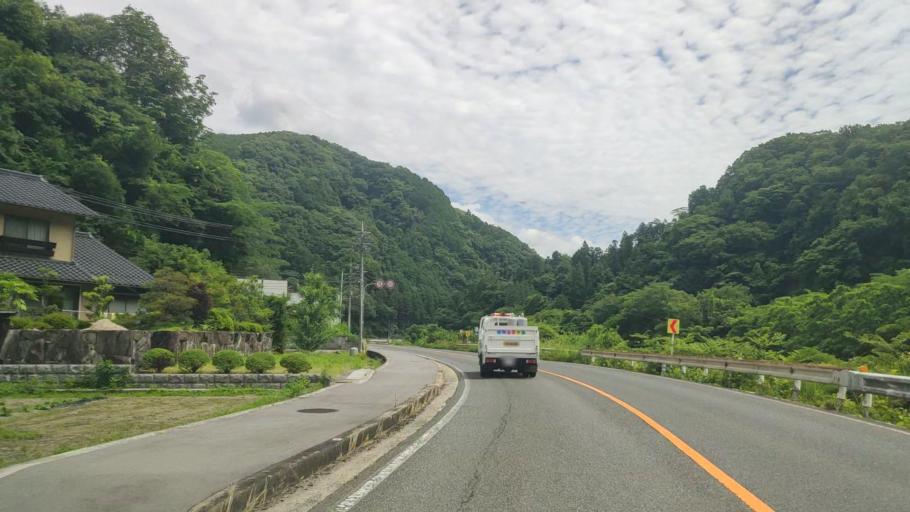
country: JP
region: Okayama
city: Niimi
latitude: 35.0707
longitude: 133.6799
